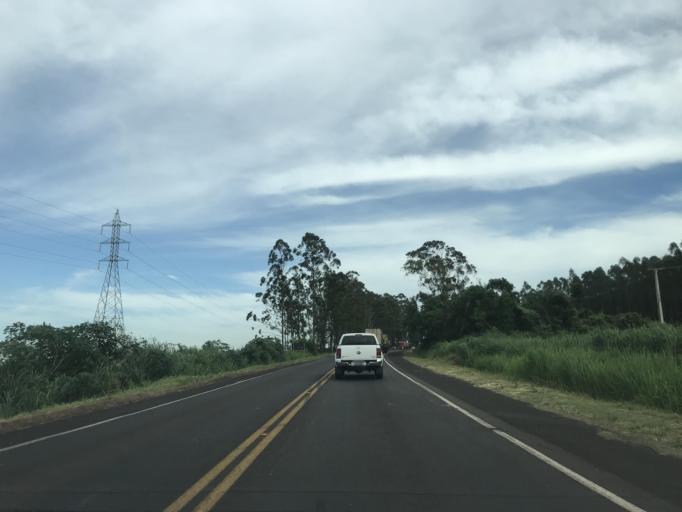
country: BR
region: Parana
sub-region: Paranavai
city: Nova Aurora
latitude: -22.9897
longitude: -52.5966
